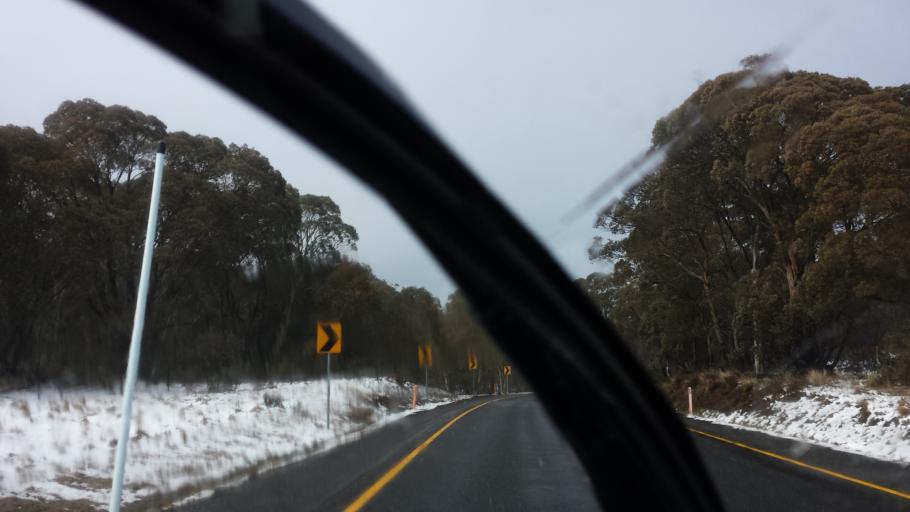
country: AU
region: Victoria
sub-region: Alpine
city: Mount Beauty
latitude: -37.0358
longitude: 147.3046
